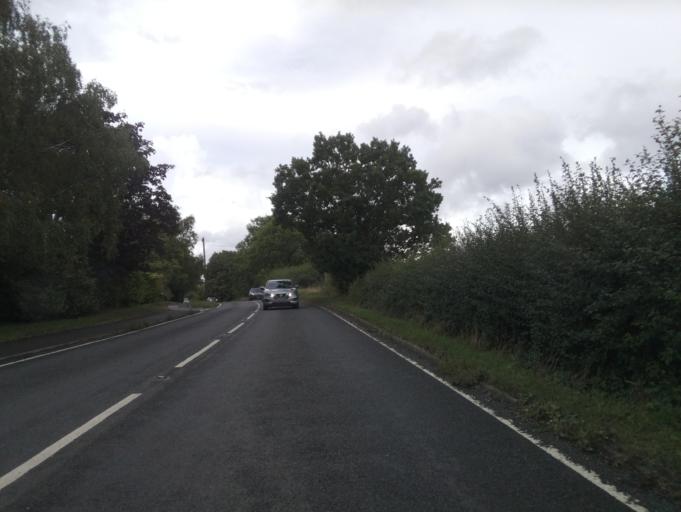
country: GB
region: England
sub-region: Worcestershire
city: Droitwich
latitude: 52.3126
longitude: -2.1774
